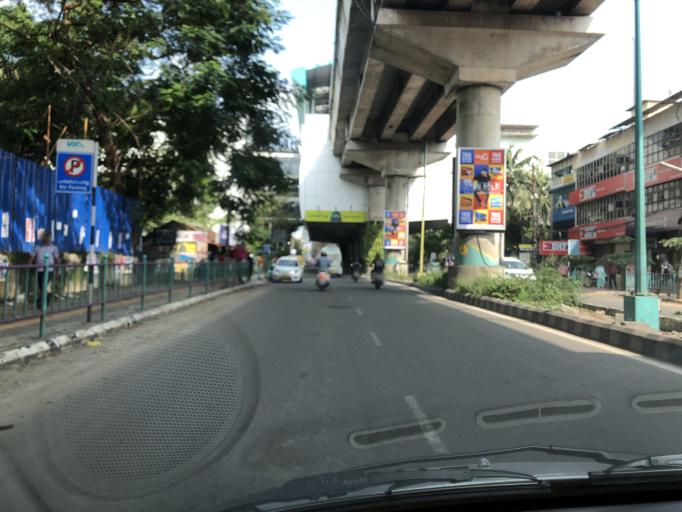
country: IN
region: Kerala
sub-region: Ernakulam
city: Elur
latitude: 10.0055
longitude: 76.3050
